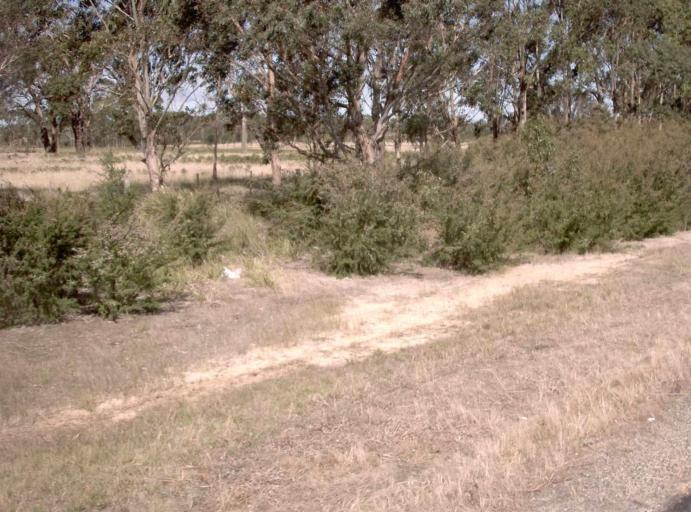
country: AU
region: Victoria
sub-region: Wellington
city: Sale
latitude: -38.3421
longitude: 147.1677
